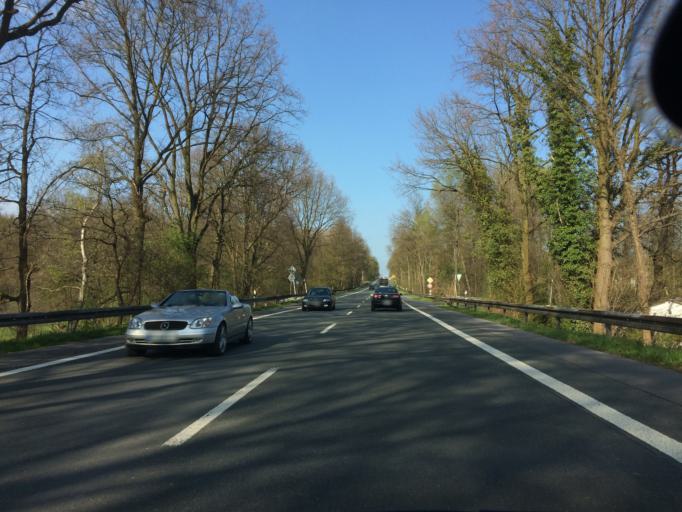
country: DE
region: North Rhine-Westphalia
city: Herten
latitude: 51.5629
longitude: 7.1219
